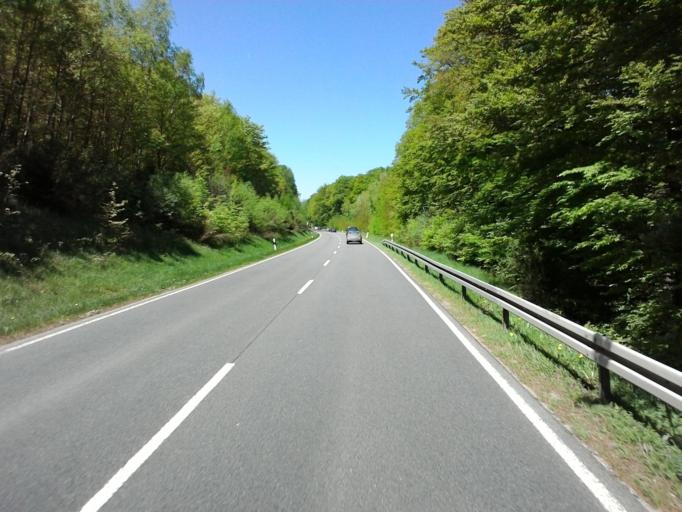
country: DE
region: Bavaria
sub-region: Regierungsbezirk Unterfranken
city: Neuhutten
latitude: 49.9836
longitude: 9.4087
